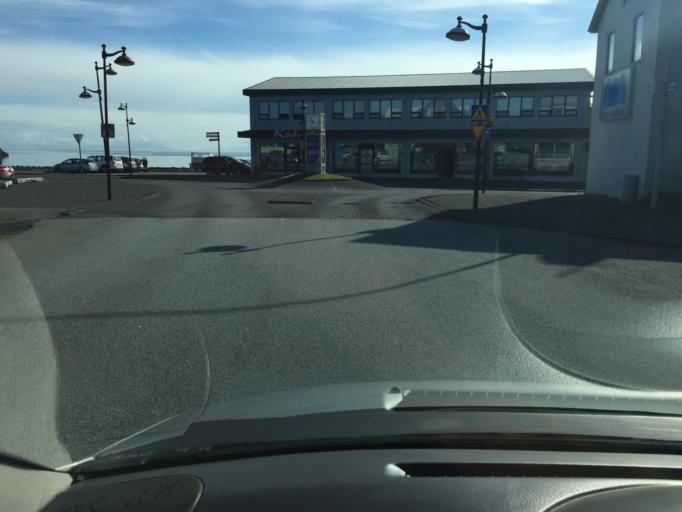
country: IS
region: Southern Peninsula
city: Reykjanesbaer
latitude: 64.0045
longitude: -22.5567
